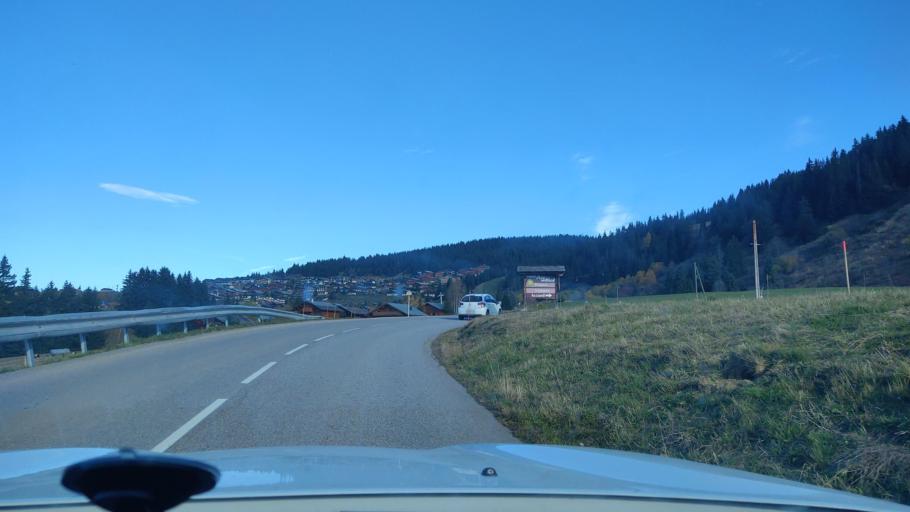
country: FR
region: Rhone-Alpes
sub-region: Departement de la Savoie
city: Beaufort
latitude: 45.7478
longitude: 6.5476
